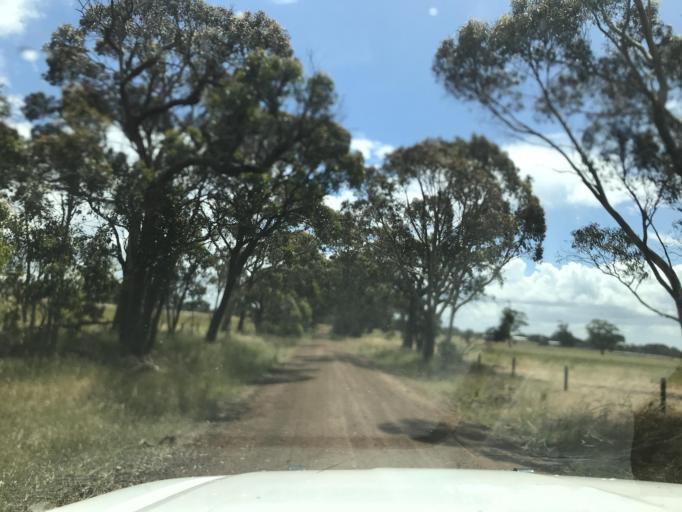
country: AU
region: South Australia
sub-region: Wattle Range
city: Penola
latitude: -37.1244
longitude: 141.2905
